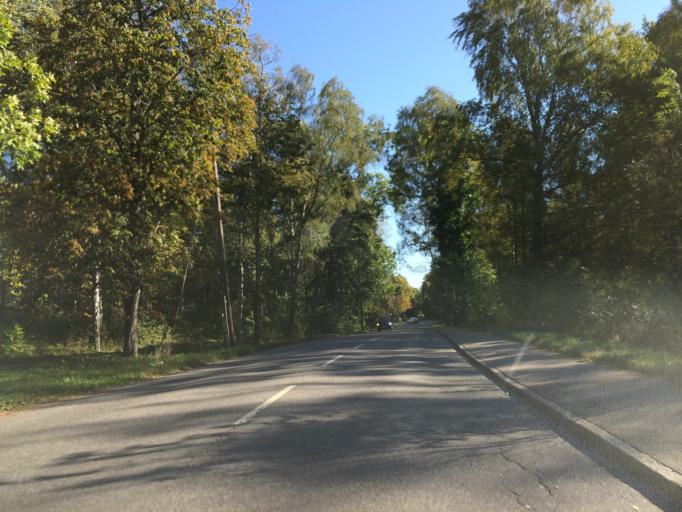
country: SE
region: Stockholm
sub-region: Lidingo
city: Lidingoe
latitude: 59.3336
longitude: 18.1258
